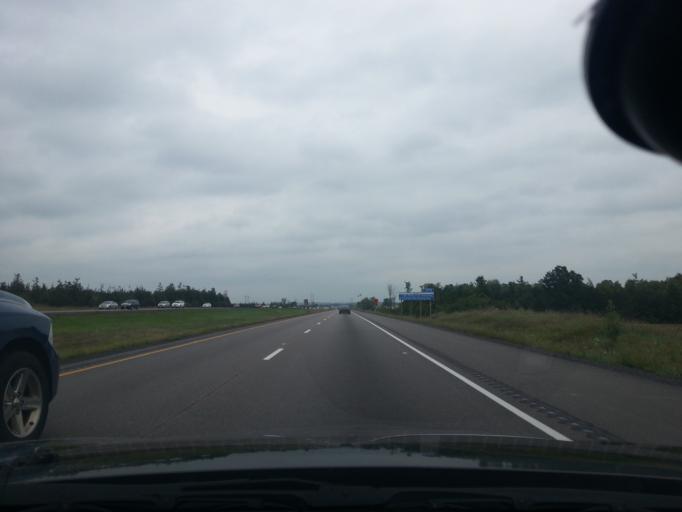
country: CA
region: Ontario
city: Napanee Downtown
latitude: 44.2577
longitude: -76.9844
